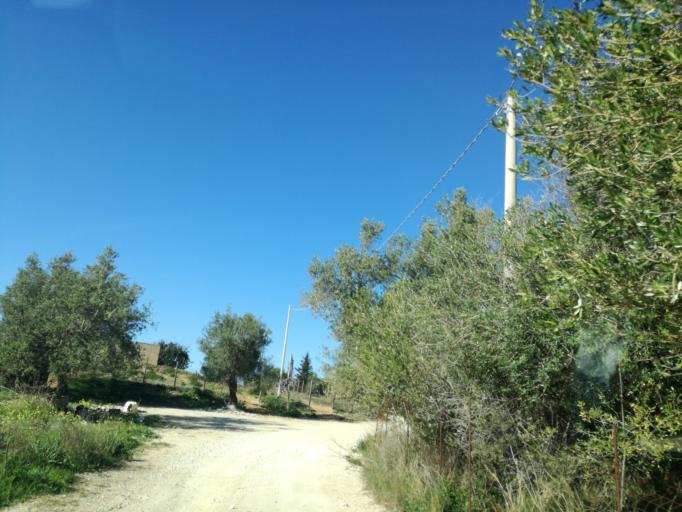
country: IT
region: Sicily
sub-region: Provincia di Caltanissetta
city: Niscemi
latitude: 37.0569
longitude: 14.3607
